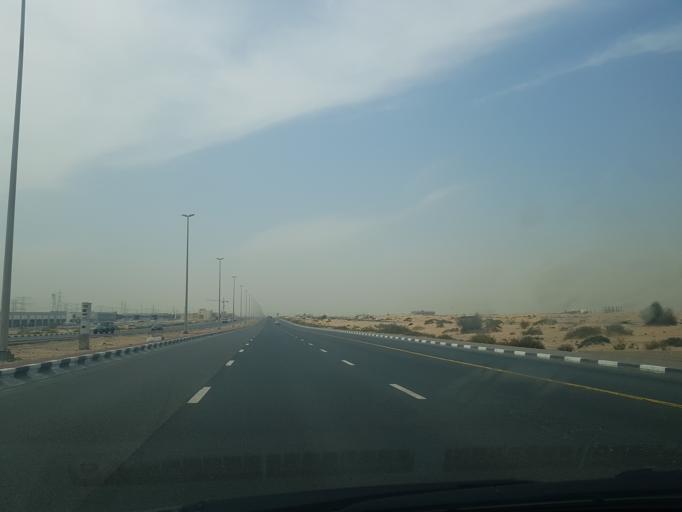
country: AE
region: Ash Shariqah
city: Sharjah
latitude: 25.2541
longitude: 55.5250
